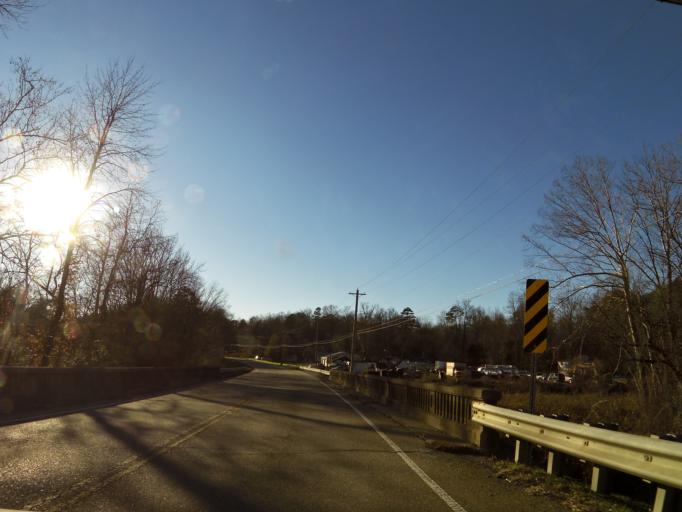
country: US
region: Tennessee
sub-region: Anderson County
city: Oak Ridge
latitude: 36.0614
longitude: -84.2304
